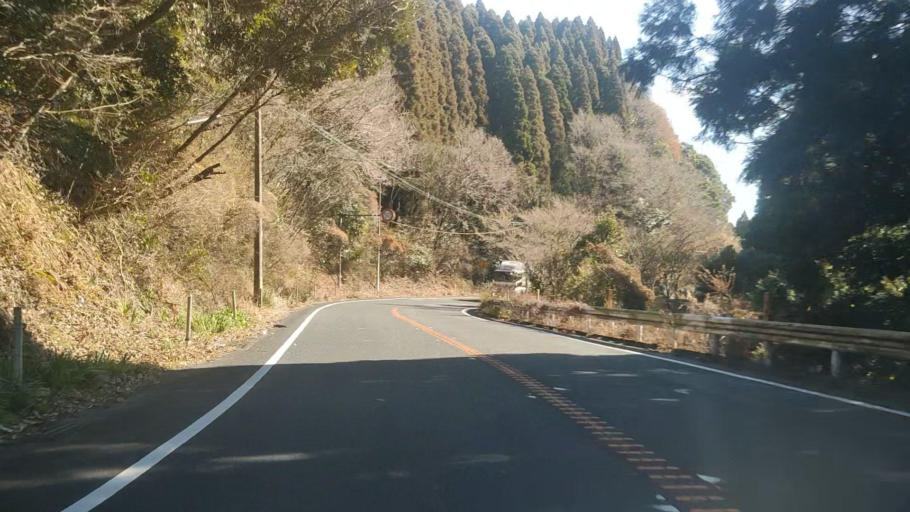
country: JP
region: Kagoshima
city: Sueyoshicho-ninokata
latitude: 31.6625
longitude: 130.8851
